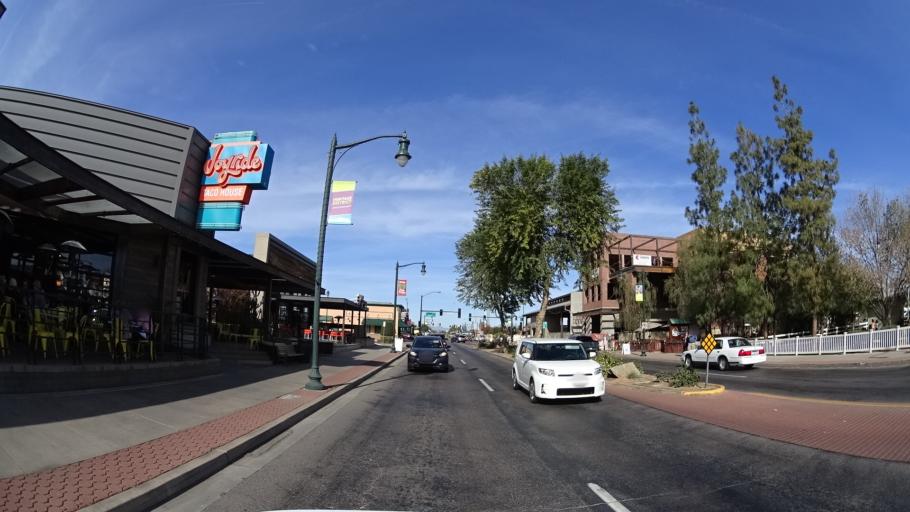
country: US
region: Arizona
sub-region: Maricopa County
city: Gilbert
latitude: 33.3552
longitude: -111.7898
